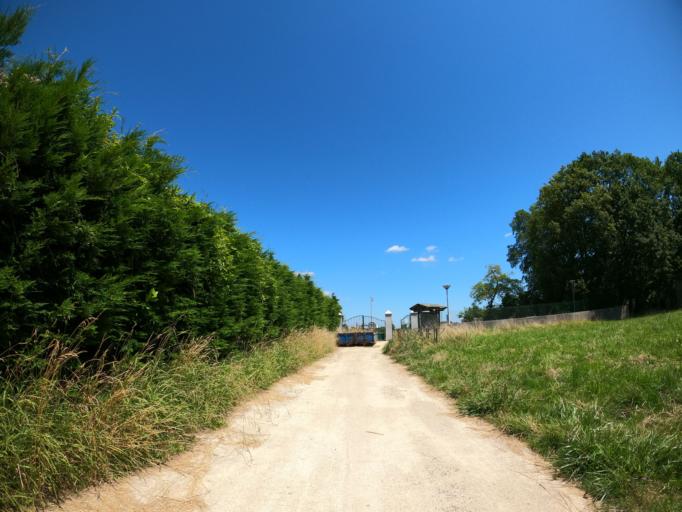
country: FR
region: Aquitaine
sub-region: Departement des Pyrenees-Atlantiques
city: Boucau
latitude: 43.5266
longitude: -1.4510
